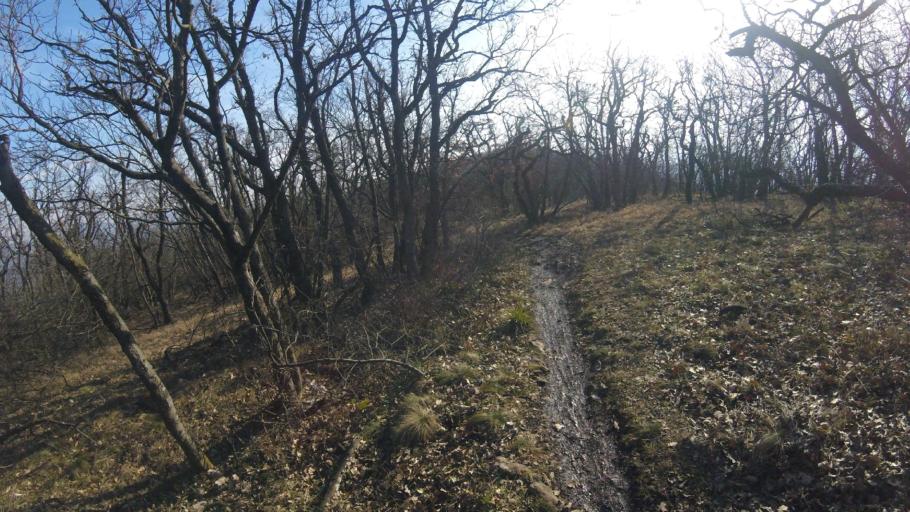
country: HU
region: Pest
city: Pilisszentkereszt
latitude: 47.6628
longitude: 18.9208
